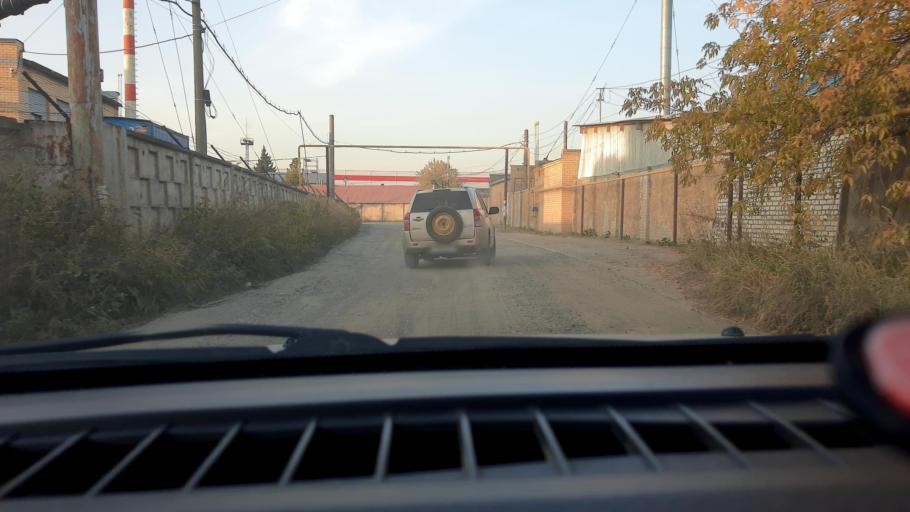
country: RU
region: Nizjnij Novgorod
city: Gorbatovka
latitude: 56.3067
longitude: 43.8291
